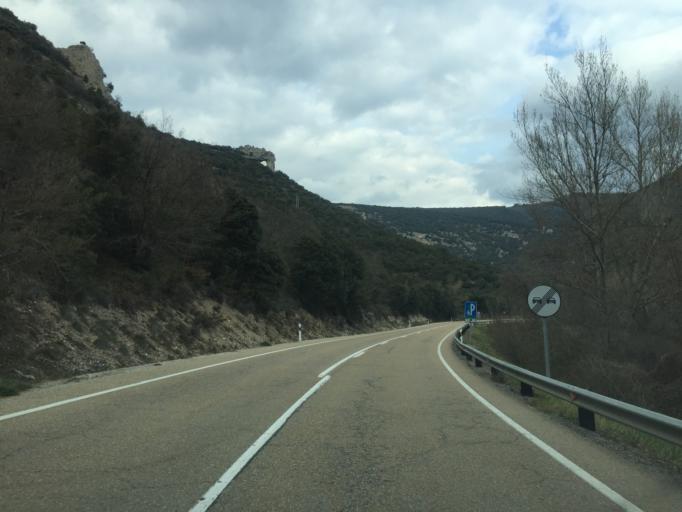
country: ES
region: Castille and Leon
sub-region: Provincia de Burgos
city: Tubilla del Agua
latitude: 42.7451
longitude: -3.8061
